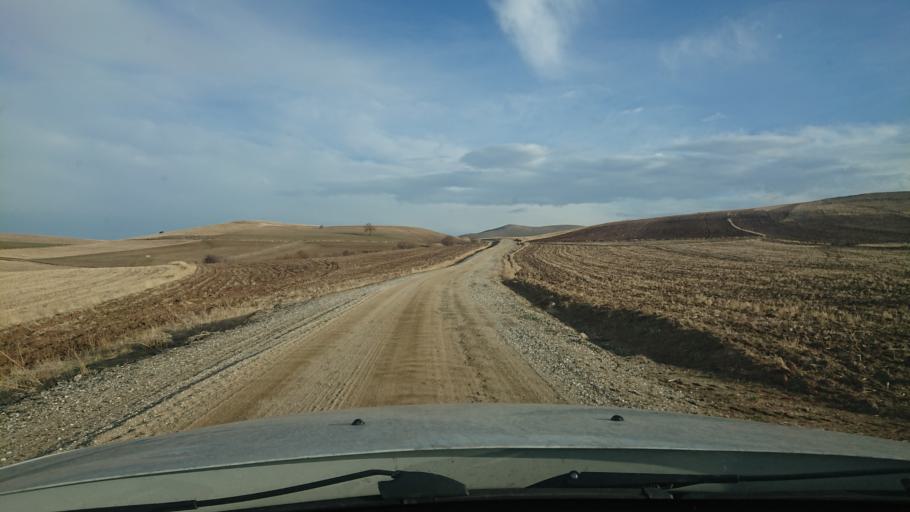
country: TR
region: Aksaray
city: Acipinar
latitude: 38.6939
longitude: 33.8703
